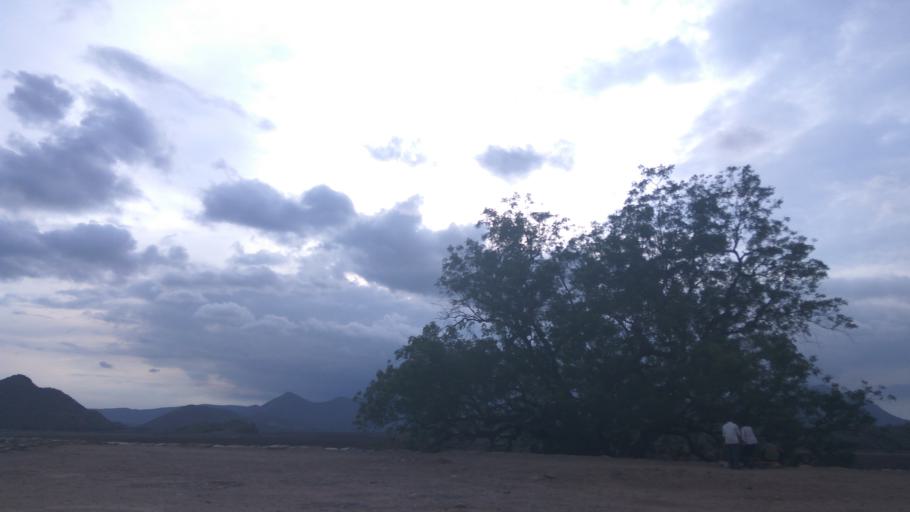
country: IN
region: Andhra Pradesh
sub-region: Prakasam
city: Cumbum
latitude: 15.5770
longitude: 79.0819
